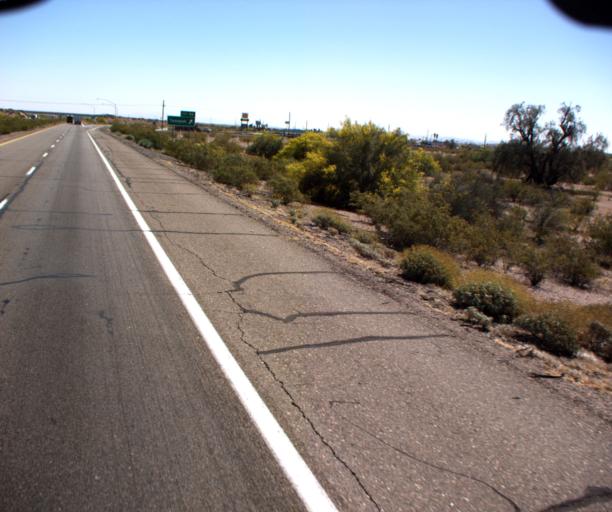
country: US
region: Arizona
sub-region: Maricopa County
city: Buckeye
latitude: 33.4988
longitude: -112.9440
